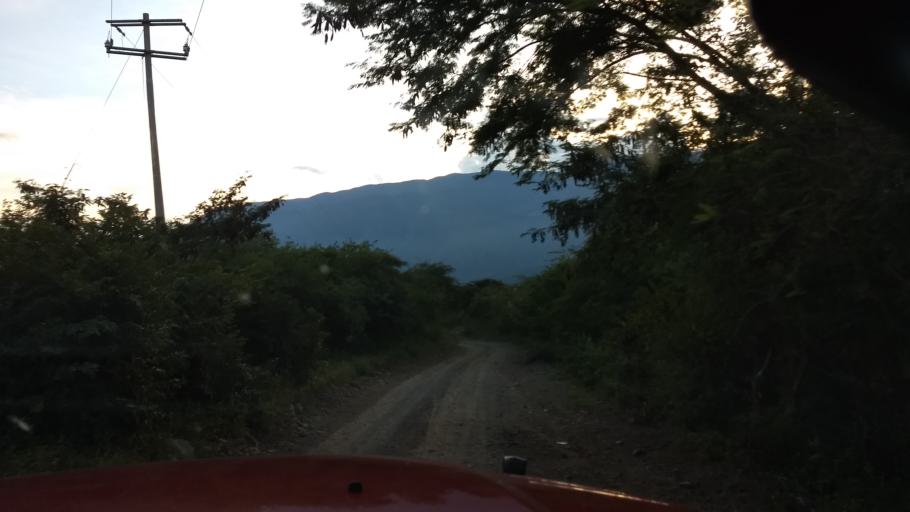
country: MX
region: Colima
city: Suchitlan
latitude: 19.4826
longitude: -103.7974
